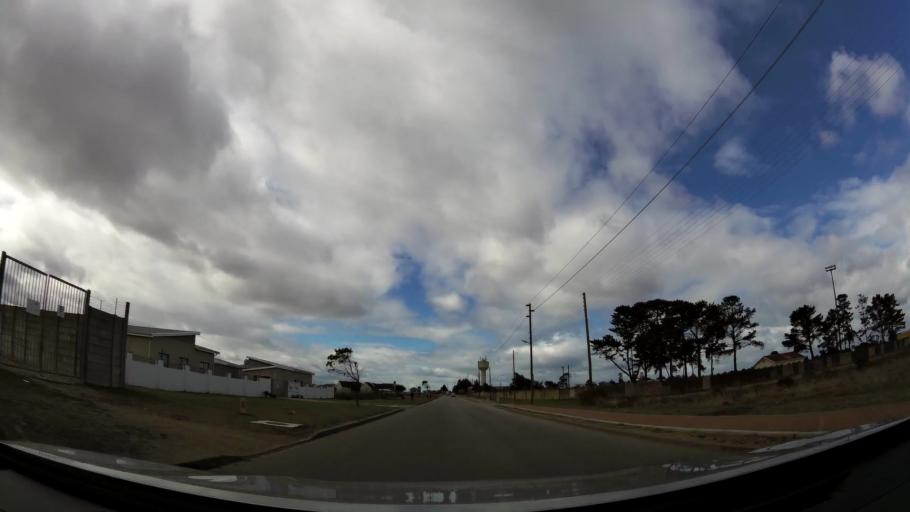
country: ZA
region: Western Cape
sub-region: Eden District Municipality
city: George
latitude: -34.0111
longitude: 22.4462
